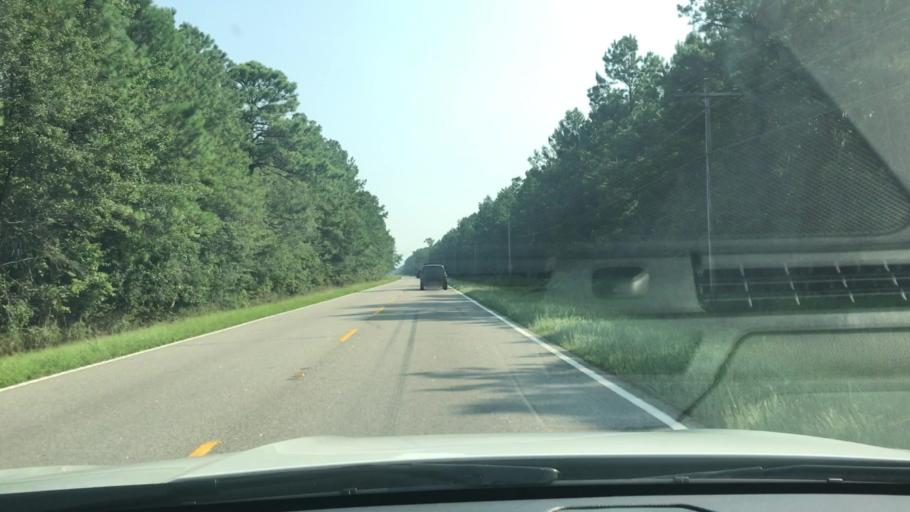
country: US
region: South Carolina
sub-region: Georgetown County
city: Georgetown
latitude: 33.5047
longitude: -79.2558
